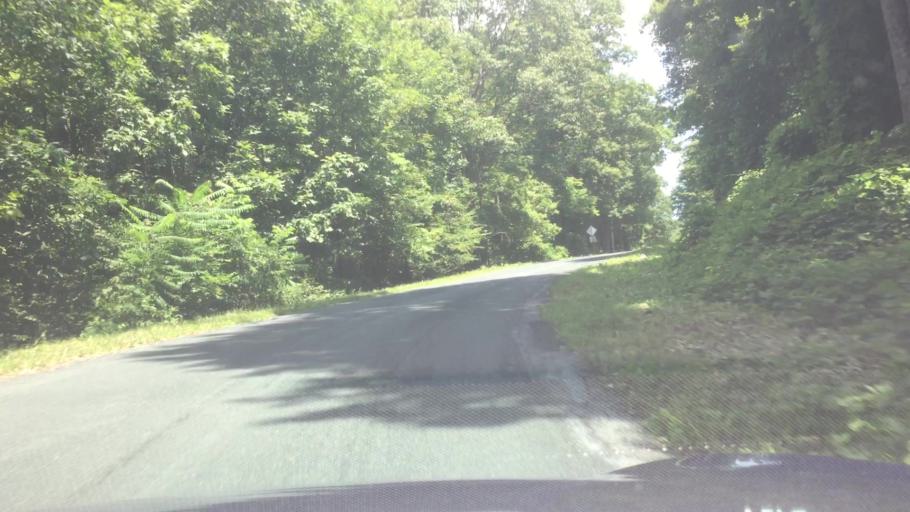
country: US
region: Virginia
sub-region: Appomattox County
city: Appomattox
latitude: 37.3266
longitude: -78.8688
